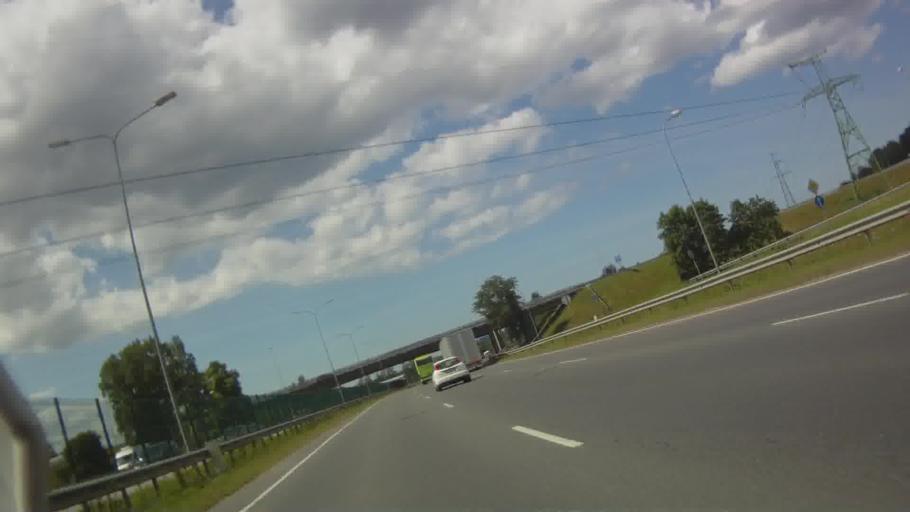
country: LV
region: Marupe
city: Marupe
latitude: 56.9308
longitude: 24.0107
